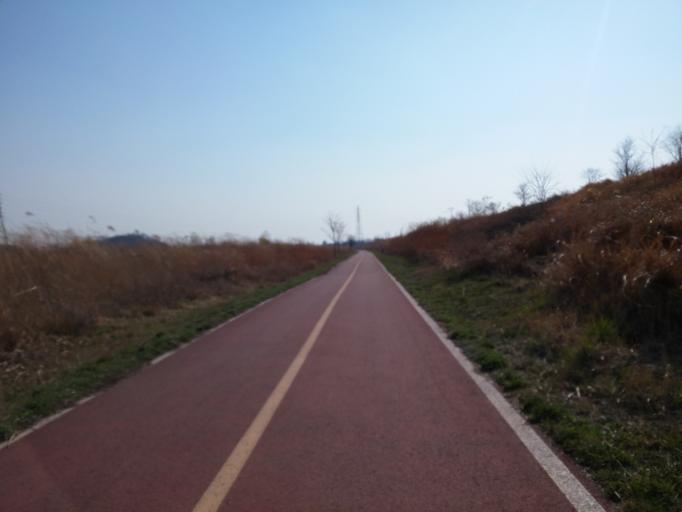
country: KR
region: Chungcheongbuk-do
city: Cheongju-si
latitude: 36.6413
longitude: 127.3606
